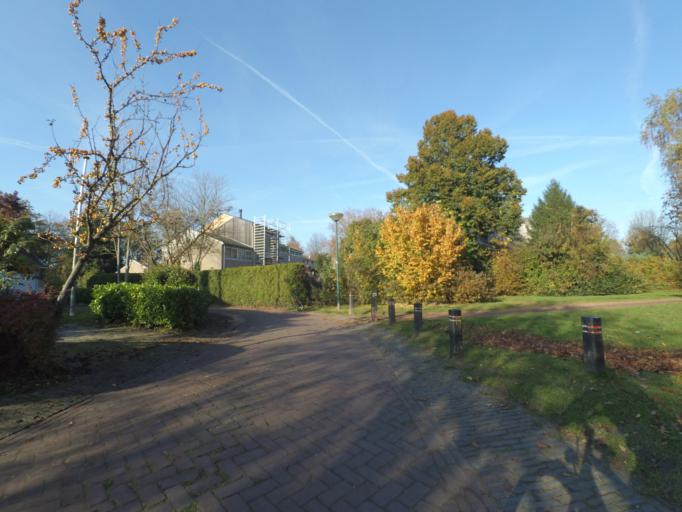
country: NL
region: Utrecht
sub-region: Gemeente Leusden
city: Leusden
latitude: 52.1340
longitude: 5.4416
